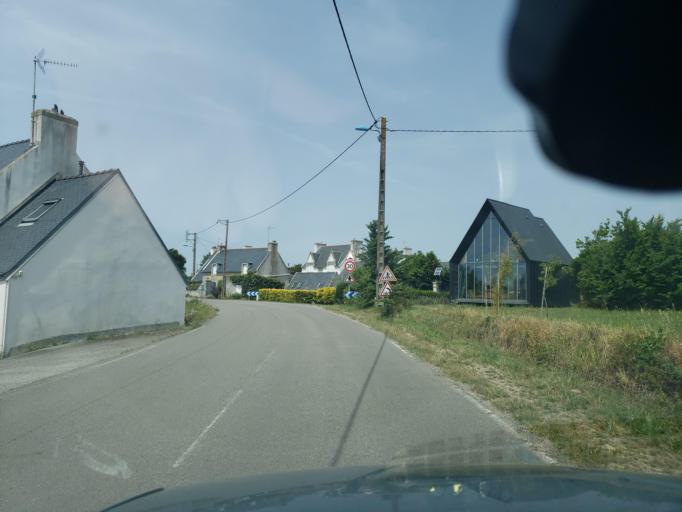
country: FR
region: Brittany
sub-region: Departement du Finistere
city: Guilvinec
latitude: 47.8067
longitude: -4.3058
